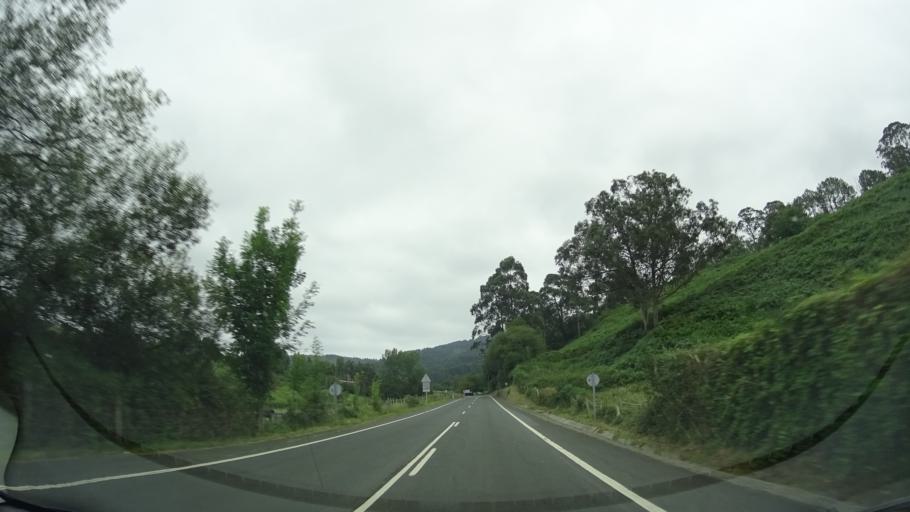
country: ES
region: Basque Country
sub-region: Bizkaia
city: Elexalde
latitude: 43.4073
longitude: -2.9048
